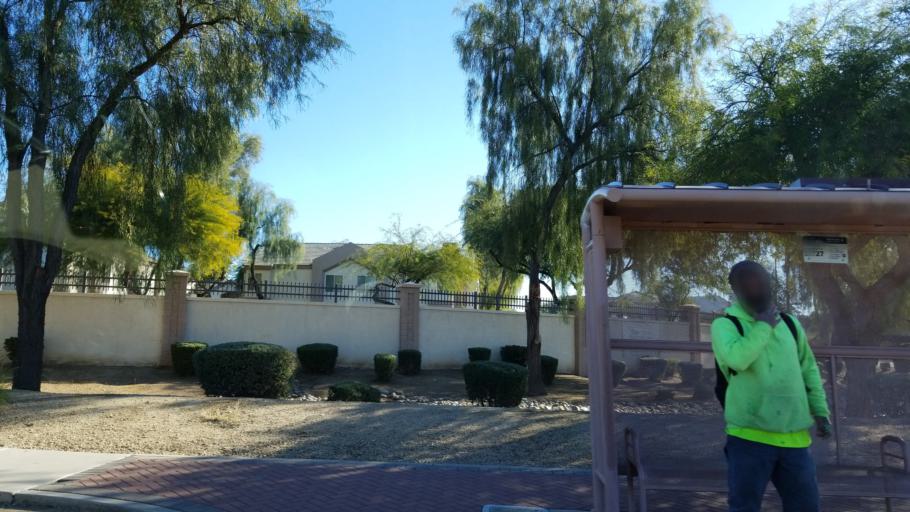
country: US
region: Arizona
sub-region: Maricopa County
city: Glendale
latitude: 33.6040
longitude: -112.1252
